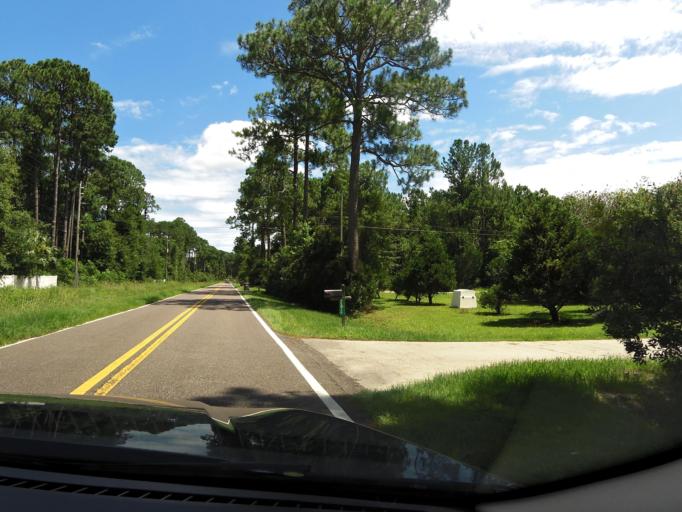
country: US
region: Georgia
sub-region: Camden County
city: St. Marys
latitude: 30.6783
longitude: -81.5327
